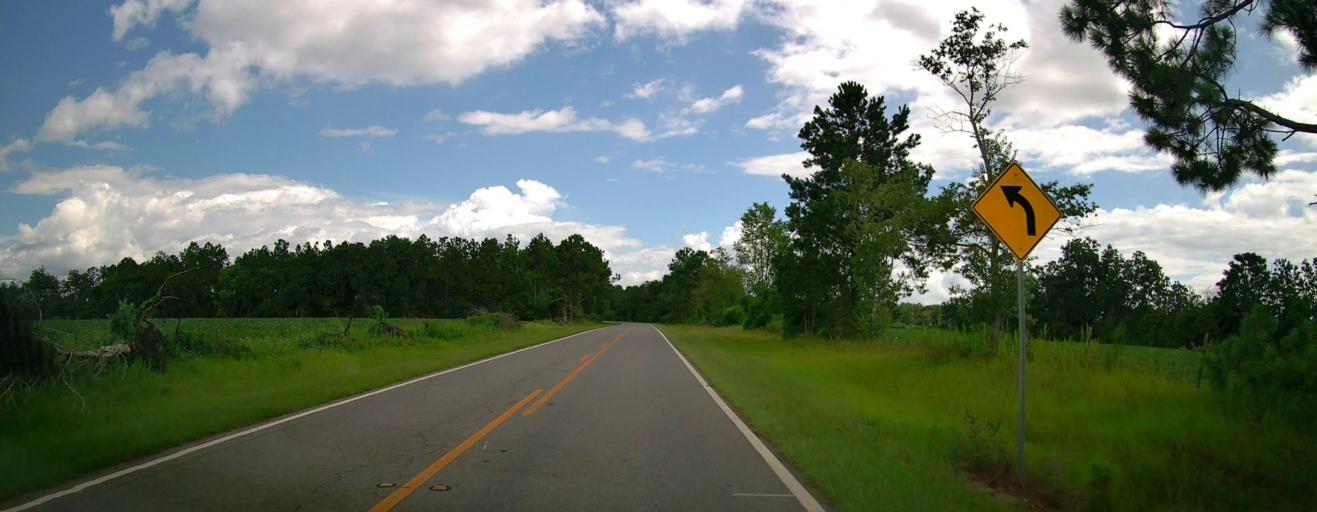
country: US
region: Georgia
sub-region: Ben Hill County
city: Fitzgerald
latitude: 31.6744
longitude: -83.1921
